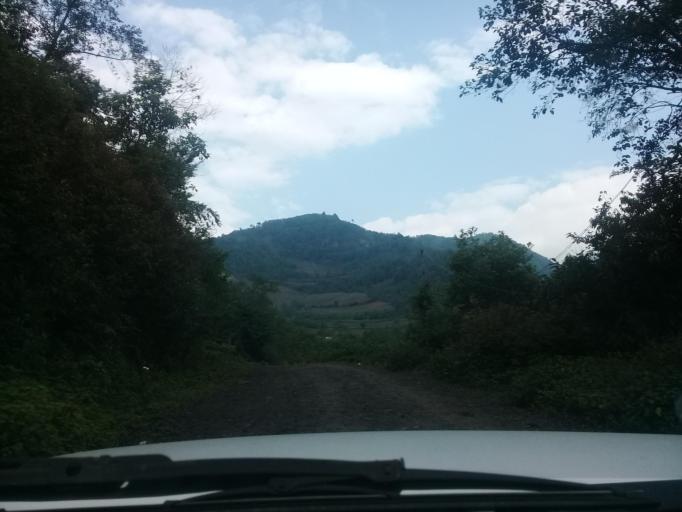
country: MX
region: Veracruz
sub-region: Mariano Escobedo
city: San Isidro el Berro
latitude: 18.9536
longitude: -97.1977
